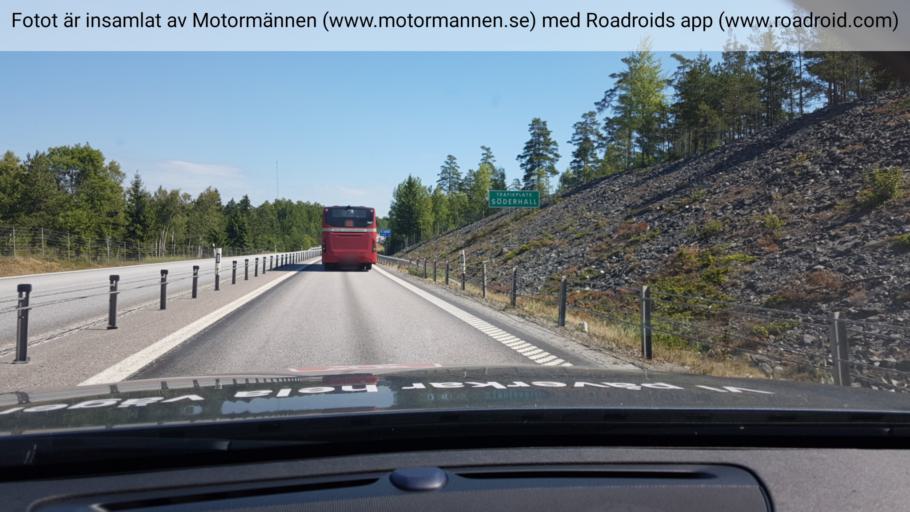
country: SE
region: Stockholm
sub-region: Norrtalje Kommun
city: Rimbo
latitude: 59.6261
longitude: 18.3122
